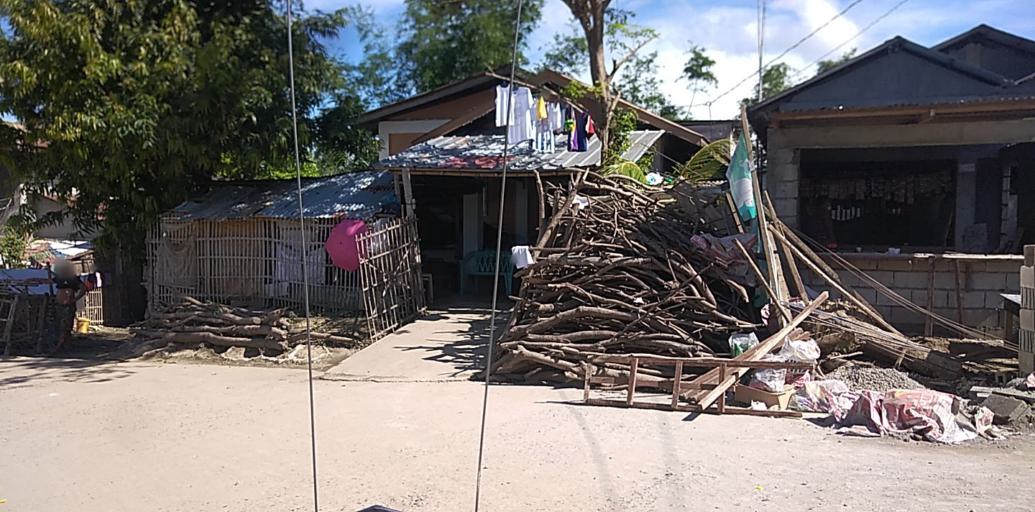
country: PH
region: Central Luzon
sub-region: Province of Pampanga
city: Candating
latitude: 15.1220
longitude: 120.8145
